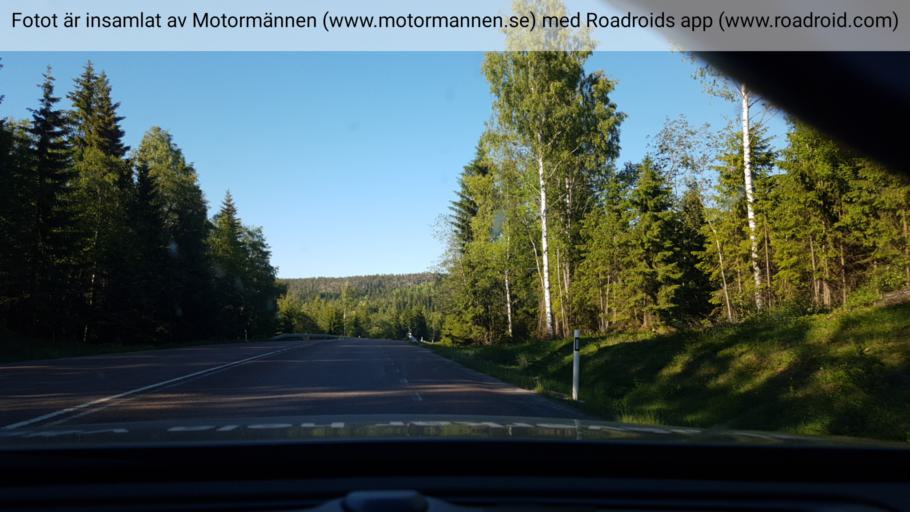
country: SE
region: Vaesternorrland
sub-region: Haernoesands Kommun
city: Haernoesand
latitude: 62.7003
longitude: 17.8562
